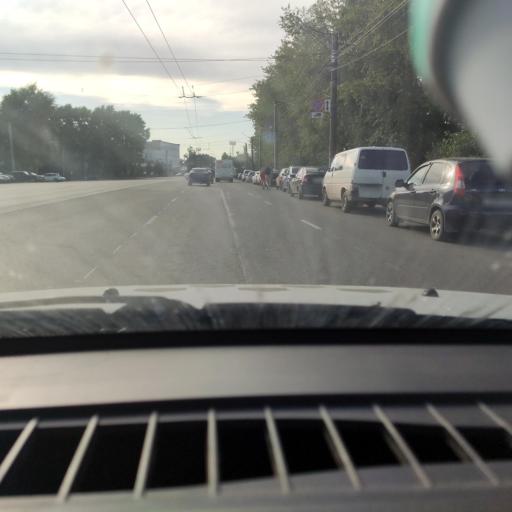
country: RU
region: Kirov
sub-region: Kirovo-Chepetskiy Rayon
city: Kirov
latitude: 58.6197
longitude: 49.6587
